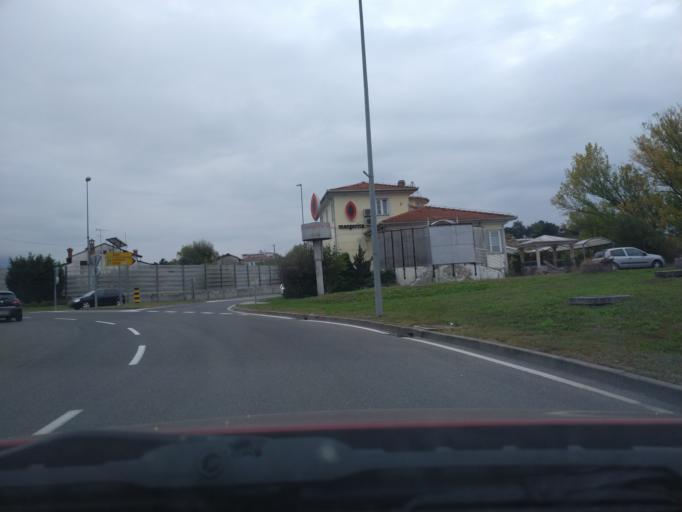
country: SI
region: Nova Gorica
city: Nova Gorica
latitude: 45.9584
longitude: 13.6521
